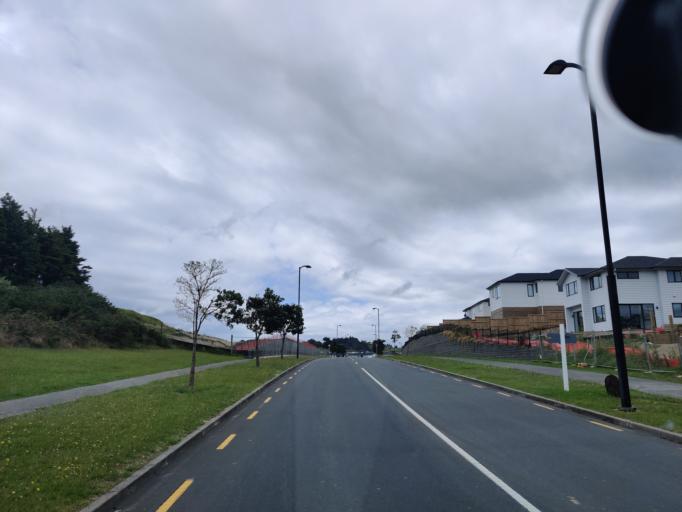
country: NZ
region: Auckland
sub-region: Auckland
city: Rothesay Bay
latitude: -36.5950
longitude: 174.6711
